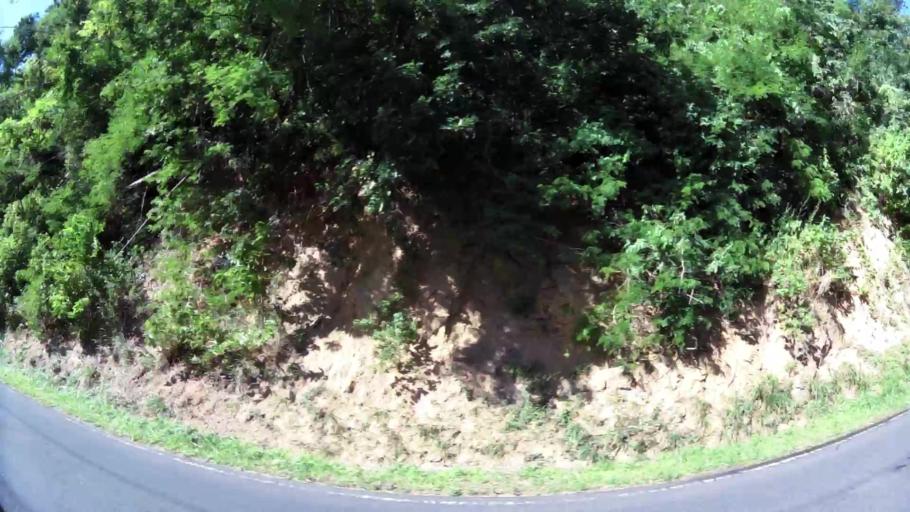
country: LC
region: Soufriere
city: Soufriere
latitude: 13.8379
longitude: -61.0538
